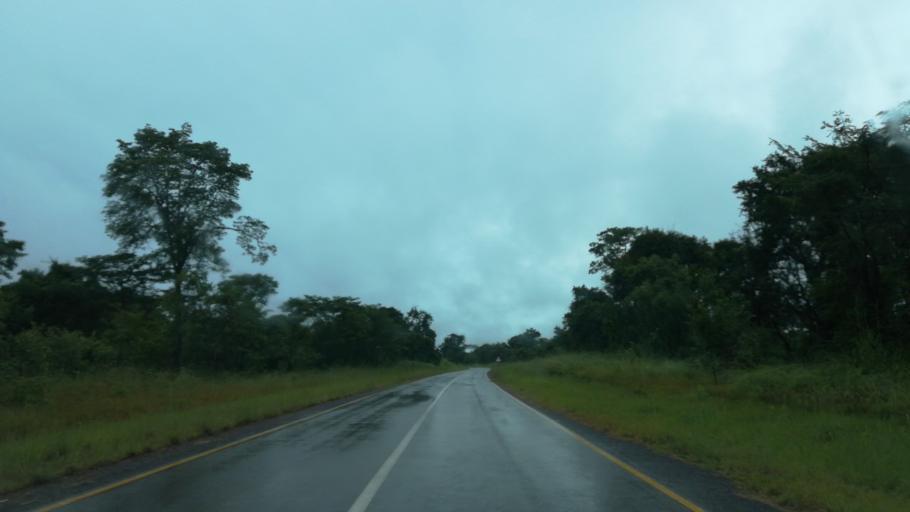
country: ZM
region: Luapula
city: Mwense
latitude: -10.8390
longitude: 28.2309
